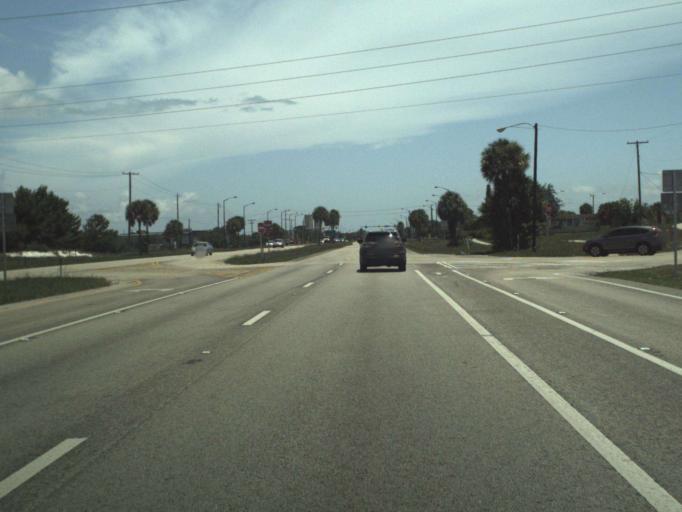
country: US
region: Florida
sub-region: Saint Lucie County
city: Fort Pierce North
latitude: 27.4734
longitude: -80.3359
